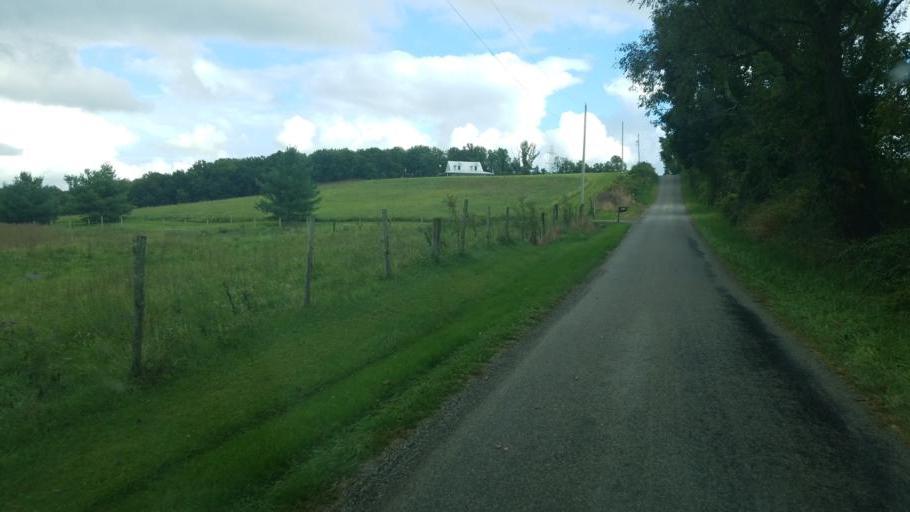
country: US
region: Ohio
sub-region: Jackson County
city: Jackson
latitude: 38.9621
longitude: -82.6329
